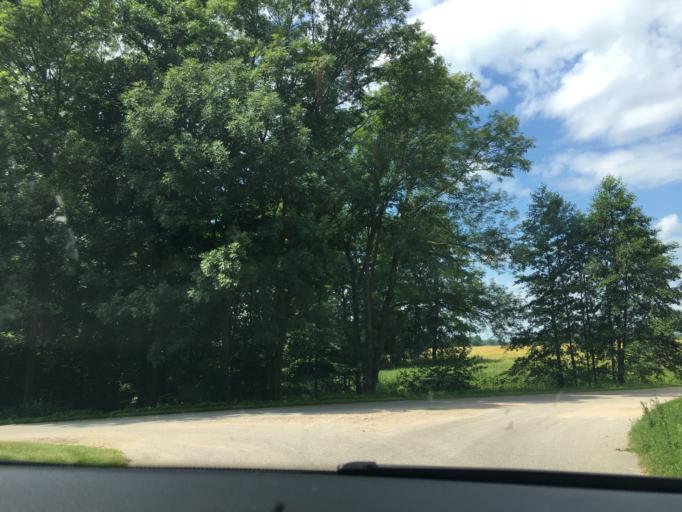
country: PL
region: Podlasie
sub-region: Powiat sejnenski
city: Krasnopol
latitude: 54.0882
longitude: 23.2448
